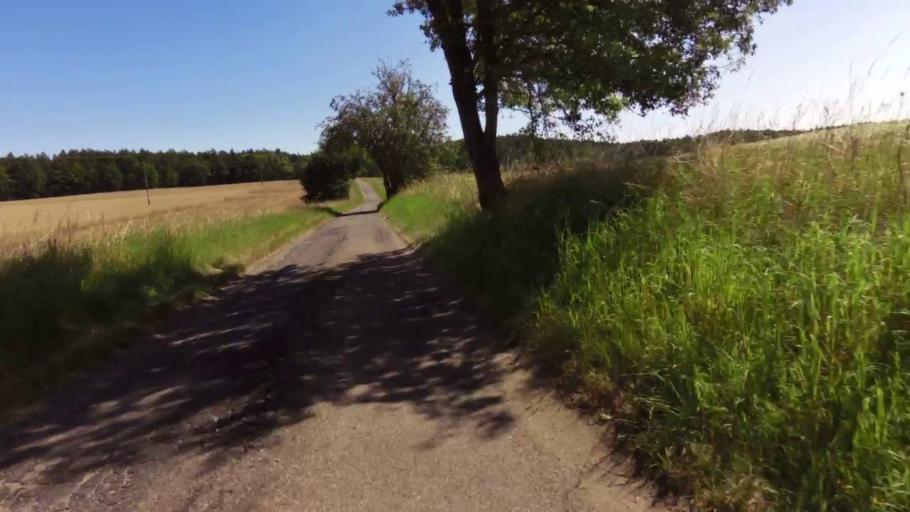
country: PL
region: West Pomeranian Voivodeship
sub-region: Powiat drawski
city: Czaplinek
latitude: 53.5247
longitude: 16.1666
